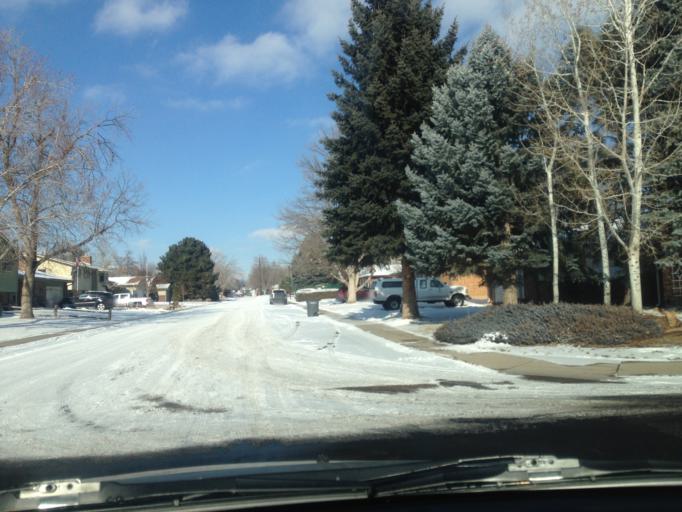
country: US
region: Colorado
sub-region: Boulder County
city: Lafayette
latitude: 39.9922
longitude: -105.0956
